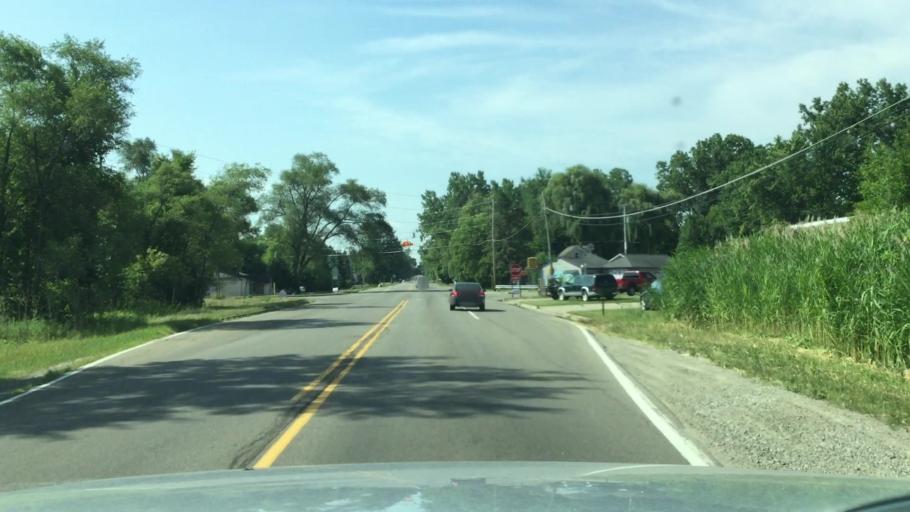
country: US
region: Michigan
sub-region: Genesee County
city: Flushing
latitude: 43.0901
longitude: -83.8135
